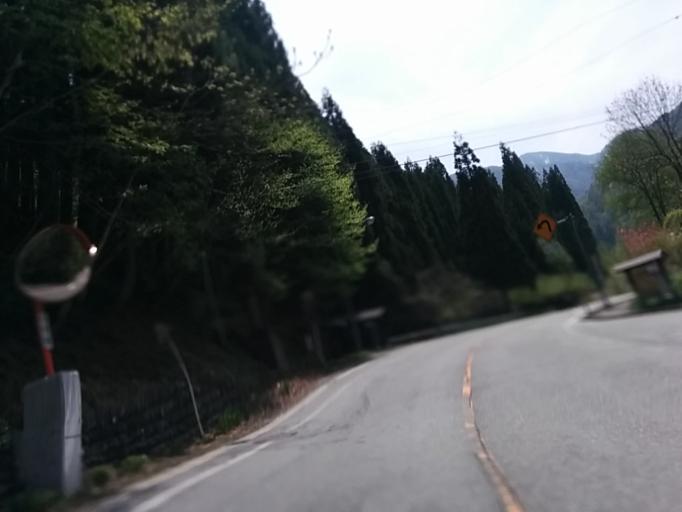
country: JP
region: Gifu
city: Takayama
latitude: 36.2321
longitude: 137.5308
